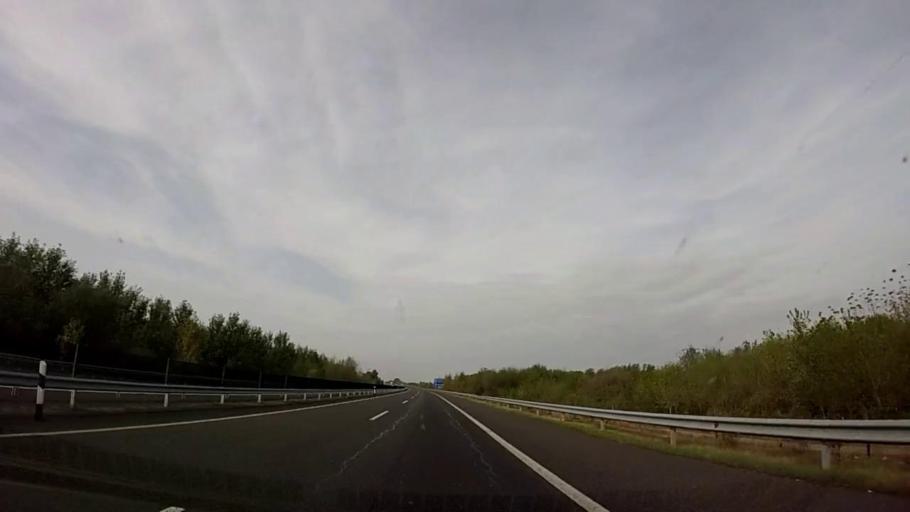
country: HU
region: Somogy
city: Balatonfenyves
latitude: 46.7029
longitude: 17.4959
